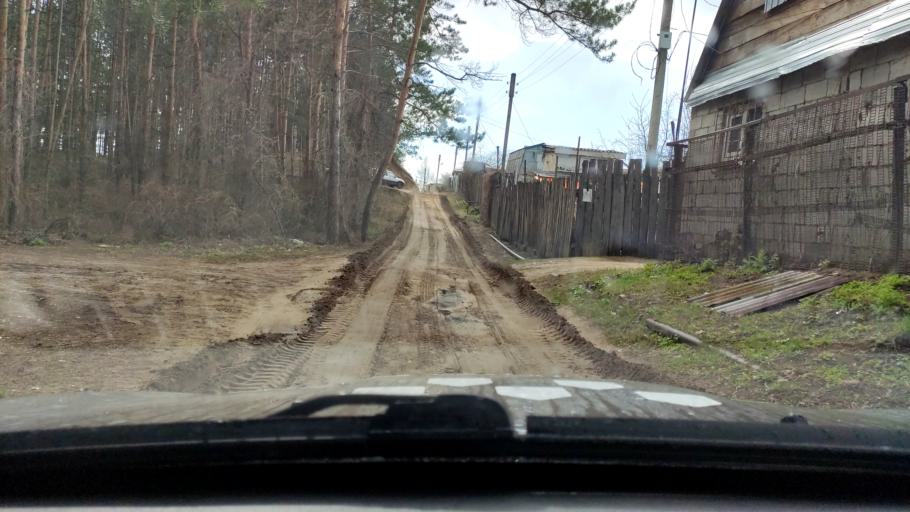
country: RU
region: Samara
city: Zhigulevsk
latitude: 53.4968
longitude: 49.5015
